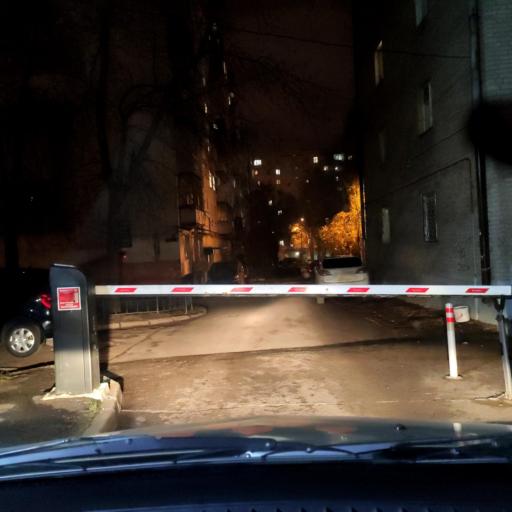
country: RU
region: Bashkortostan
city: Ufa
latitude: 54.7490
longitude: 55.9991
